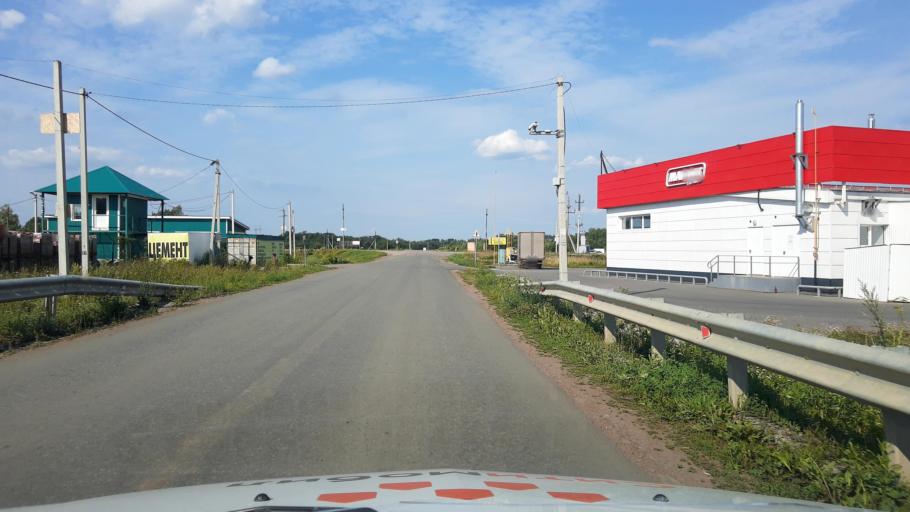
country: RU
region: Bashkortostan
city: Kabakovo
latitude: 54.6596
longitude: 56.2002
